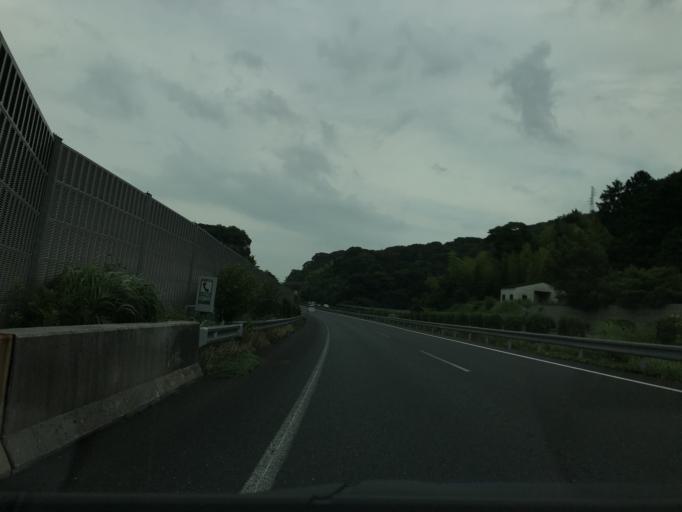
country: JP
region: Fukuoka
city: Kanda
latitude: 33.8003
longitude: 130.9524
